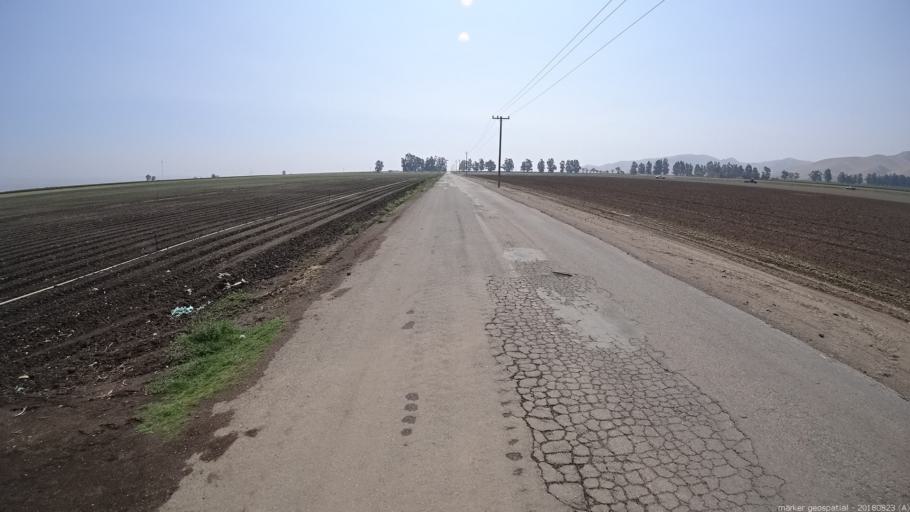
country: US
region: California
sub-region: Monterey County
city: Greenfield
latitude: 36.2824
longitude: -121.2336
